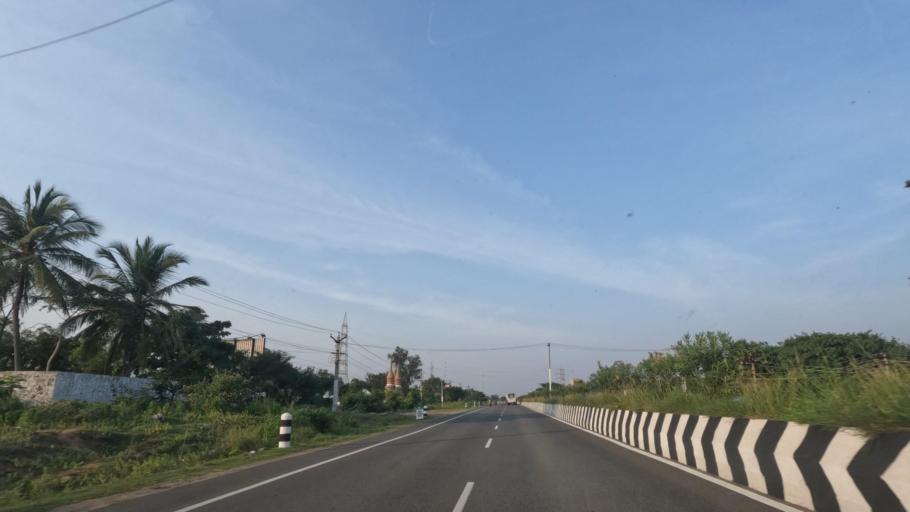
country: IN
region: Tamil Nadu
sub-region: Kancheepuram
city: Mamallapuram
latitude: 12.7004
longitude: 80.2218
